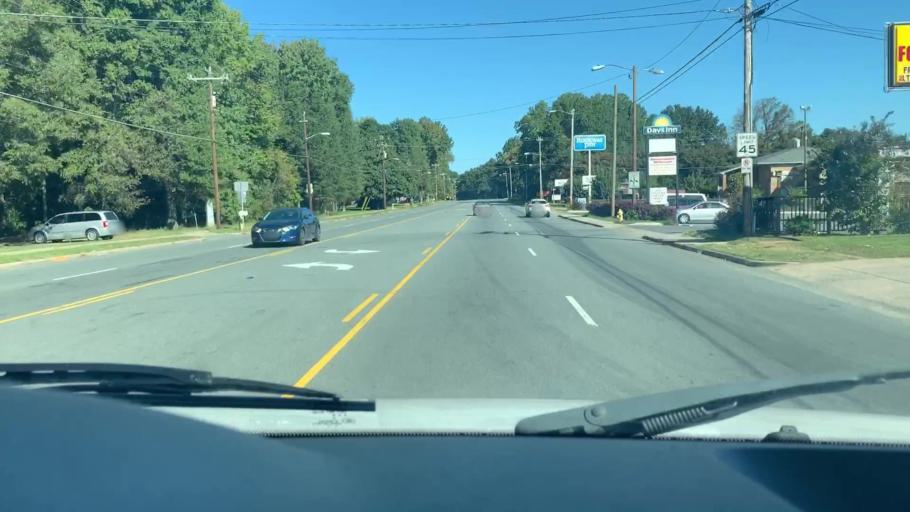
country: US
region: North Carolina
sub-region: Mecklenburg County
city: Charlotte
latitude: 35.2809
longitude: -80.7935
